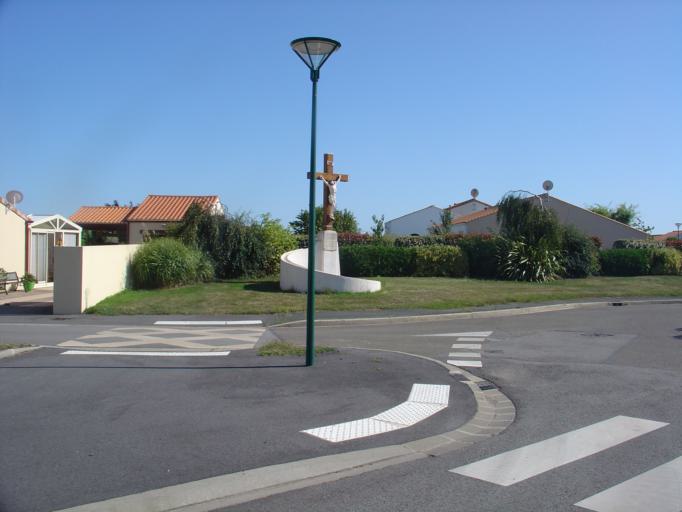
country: FR
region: Pays de la Loire
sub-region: Departement de la Vendee
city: Bretignolles-sur-Mer
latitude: 46.6436
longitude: -1.8034
